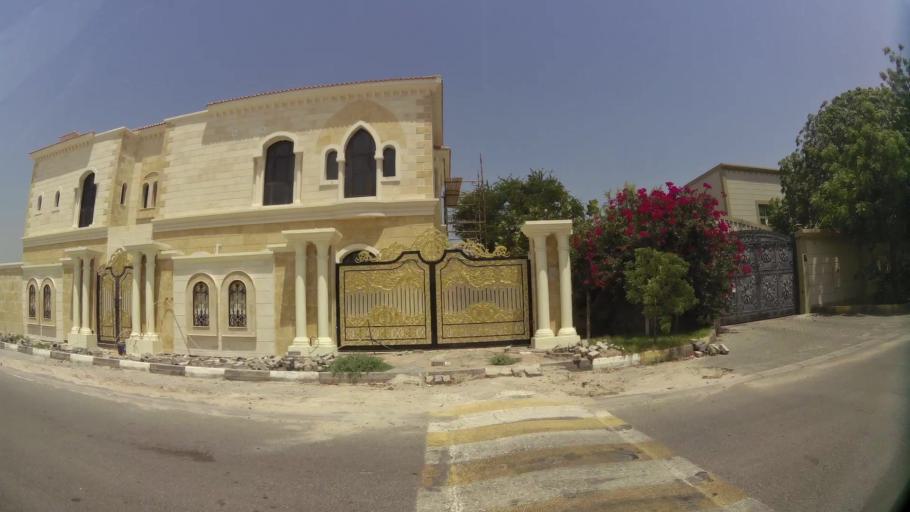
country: AE
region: Ash Shariqah
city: Sharjah
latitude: 25.3431
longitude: 55.3729
